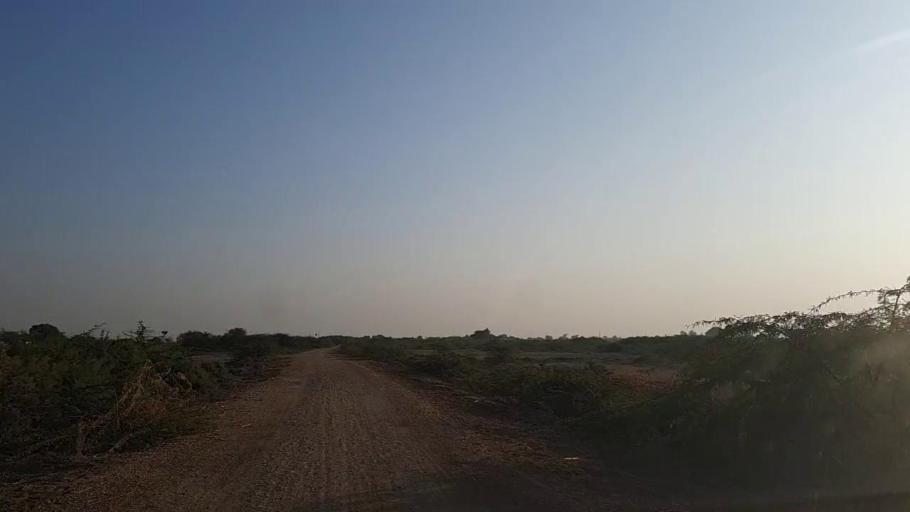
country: PK
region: Sindh
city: Naukot
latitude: 24.9277
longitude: 69.4370
